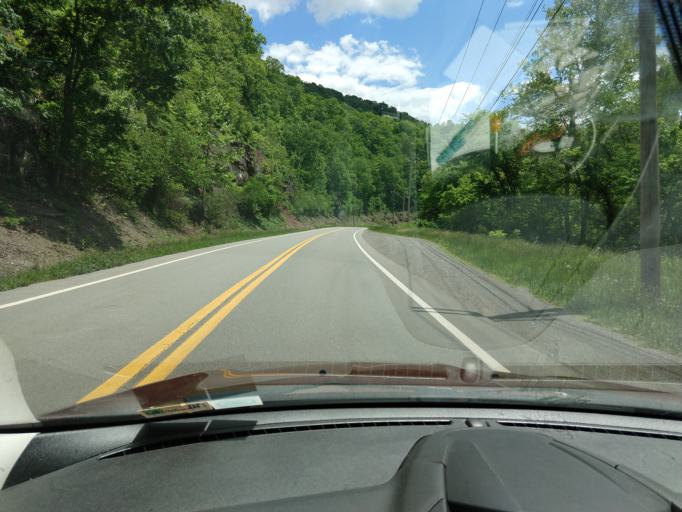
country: US
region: West Virginia
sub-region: Gilmer County
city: Glenville
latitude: 38.8894
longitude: -80.7226
